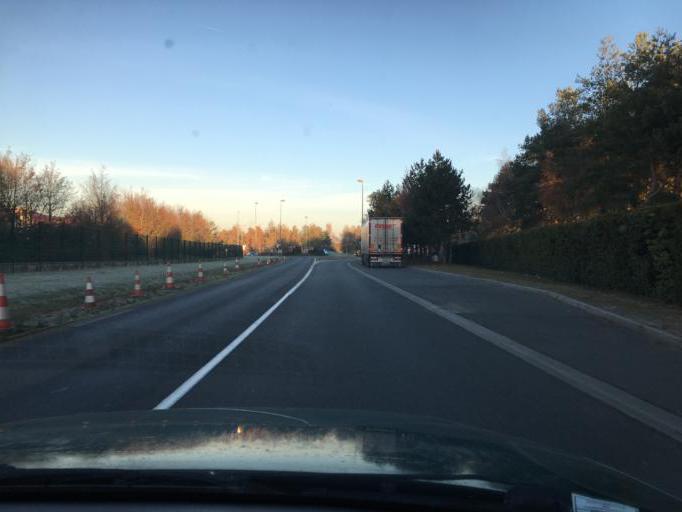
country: FR
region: Centre
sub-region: Departement du Loiret
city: Gidy
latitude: 47.9769
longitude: 1.8528
